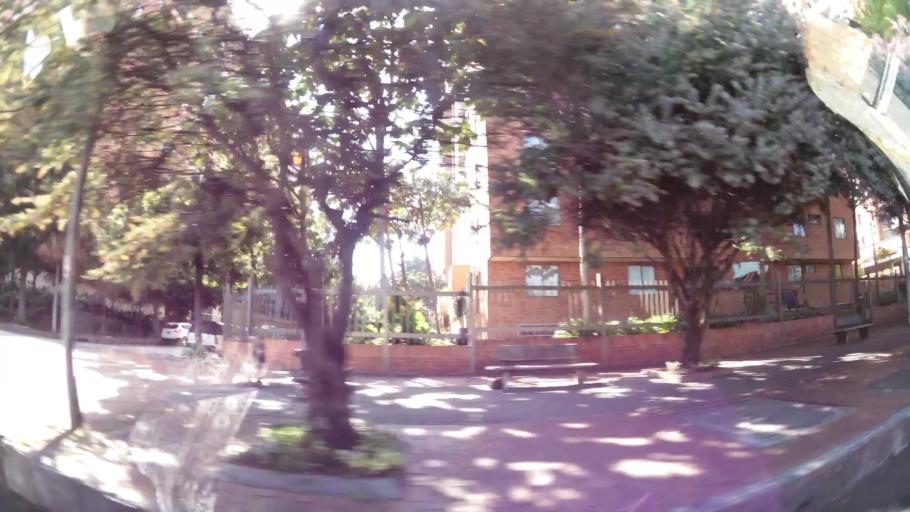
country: CO
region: Bogota D.C.
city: Barrio San Luis
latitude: 4.6876
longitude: -74.0388
